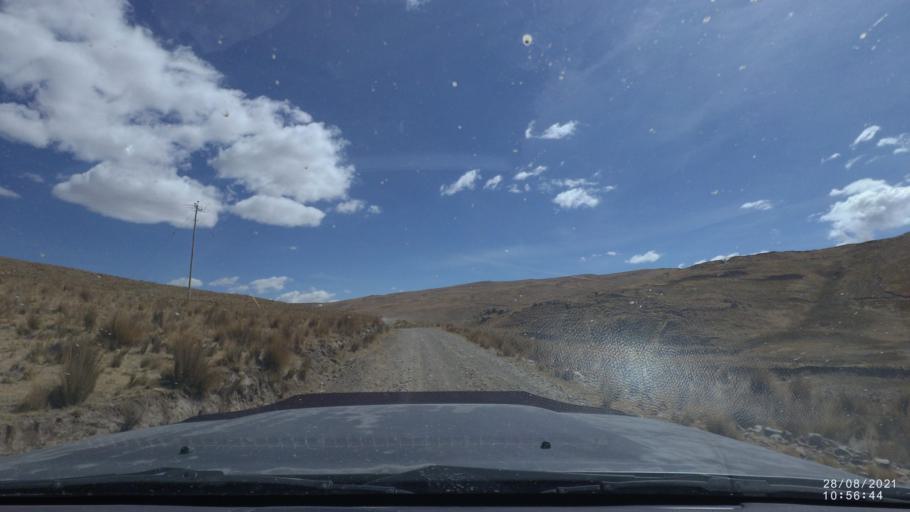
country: BO
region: Cochabamba
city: Cochabamba
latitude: -17.1918
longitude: -66.2496
